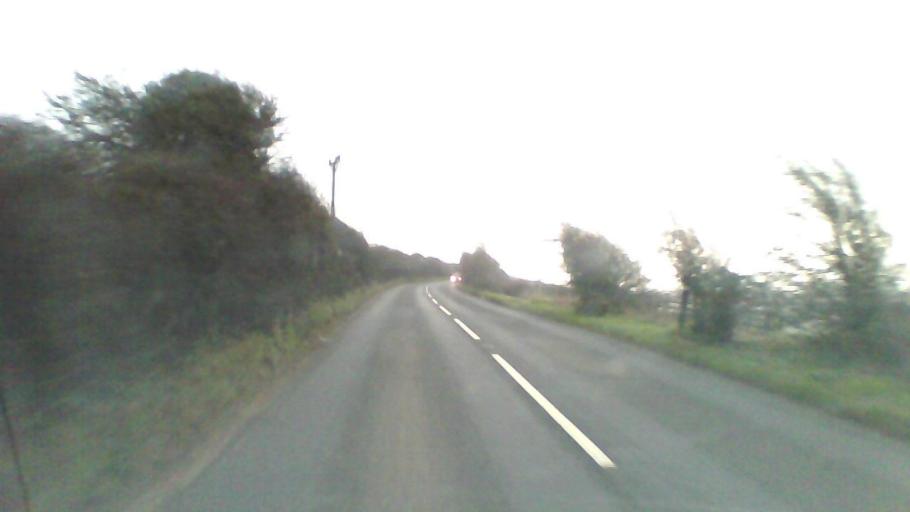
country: GB
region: England
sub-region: Isle of Wight
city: Newchurch
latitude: 50.6826
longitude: -1.2353
